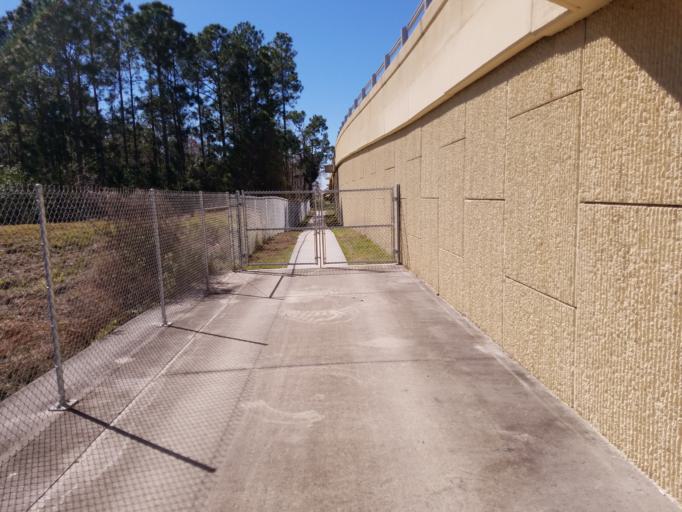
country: US
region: Florida
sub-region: Orange County
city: Tangelo Park
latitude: 28.4368
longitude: -81.4304
